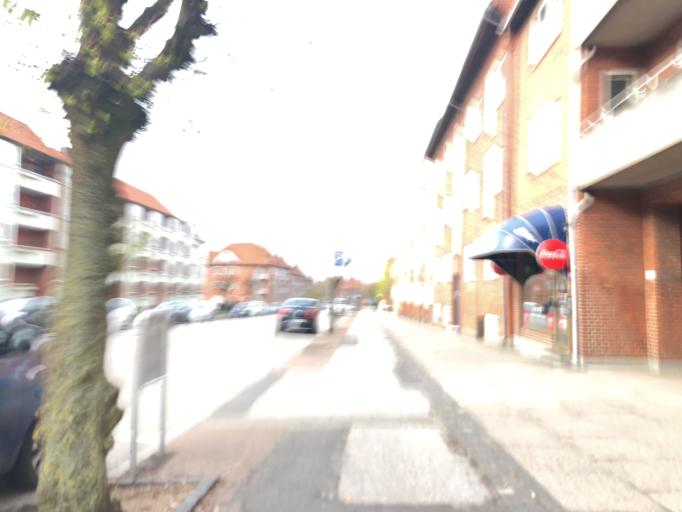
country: DK
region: Zealand
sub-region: Ringsted Kommune
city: Ringsted
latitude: 55.4406
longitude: 11.7883
